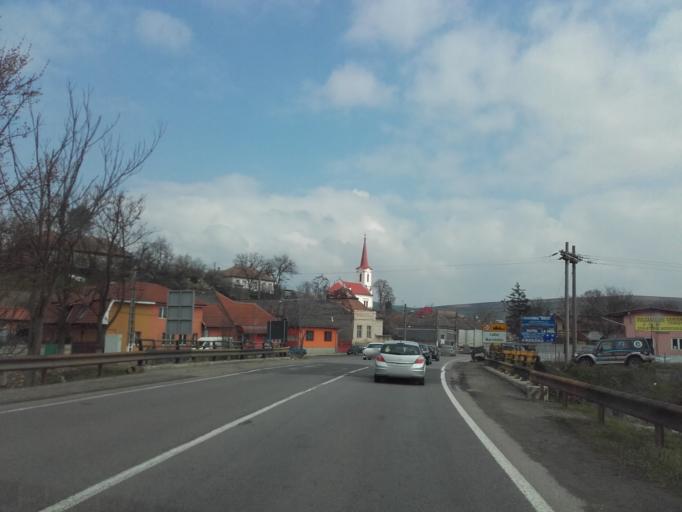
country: RO
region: Mures
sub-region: Comuna Ludus
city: Ludus
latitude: 46.4808
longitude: 24.0898
